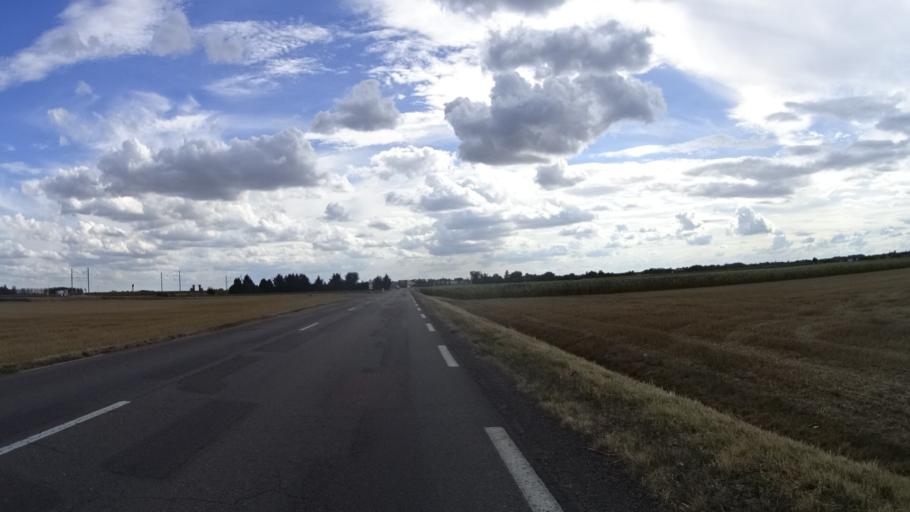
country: FR
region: Bourgogne
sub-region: Departement de la Cote-d'Or
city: Seurre
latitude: 47.0151
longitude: 5.1613
